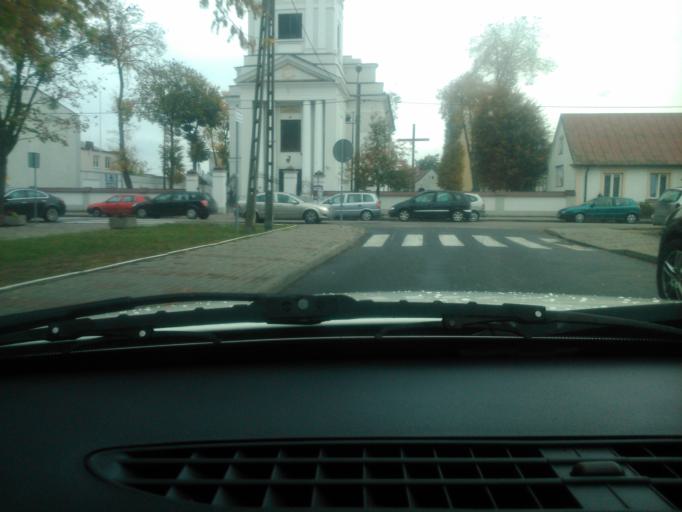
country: PL
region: Kujawsko-Pomorskie
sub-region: Powiat golubsko-dobrzynski
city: Golub-Dobrzyn
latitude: 53.1086
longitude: 19.0527
